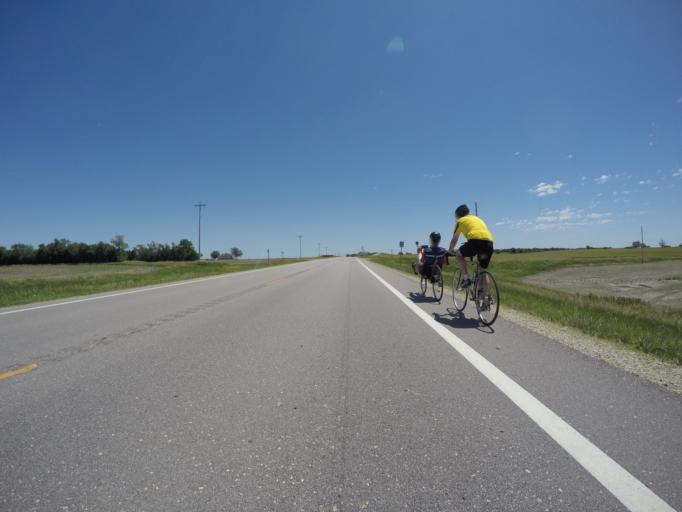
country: US
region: Kansas
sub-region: Republic County
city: Belleville
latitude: 39.8131
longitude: -97.7268
